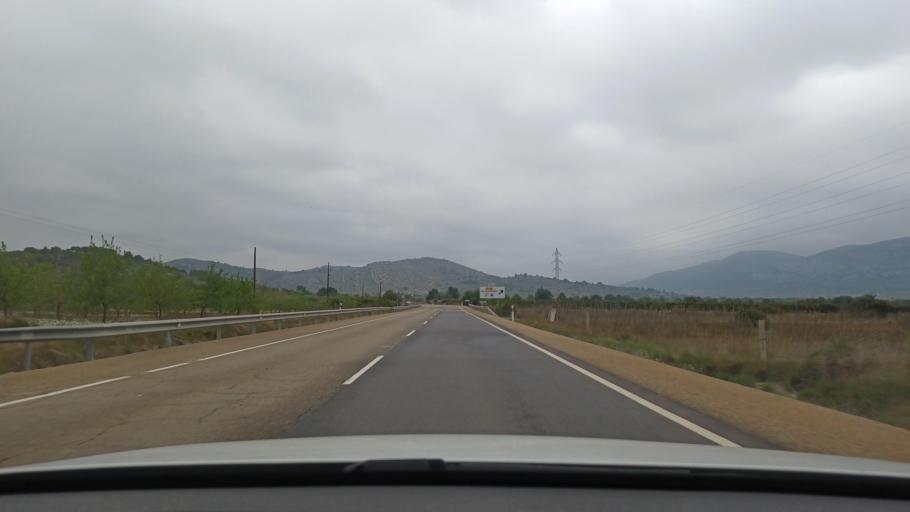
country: ES
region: Valencia
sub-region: Provincia de Castello
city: Alcala de Xivert
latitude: 40.2607
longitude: 0.2387
